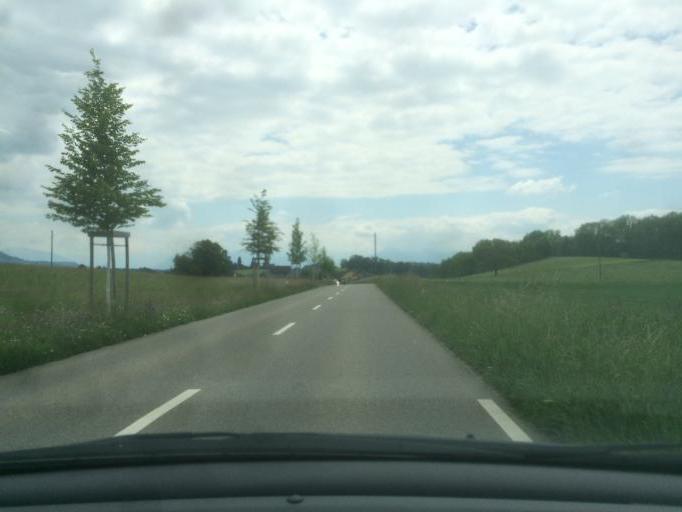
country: CH
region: Zurich
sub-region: Bezirk Hinwil
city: Wetzikon / Robenhausen
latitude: 47.3399
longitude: 8.7726
